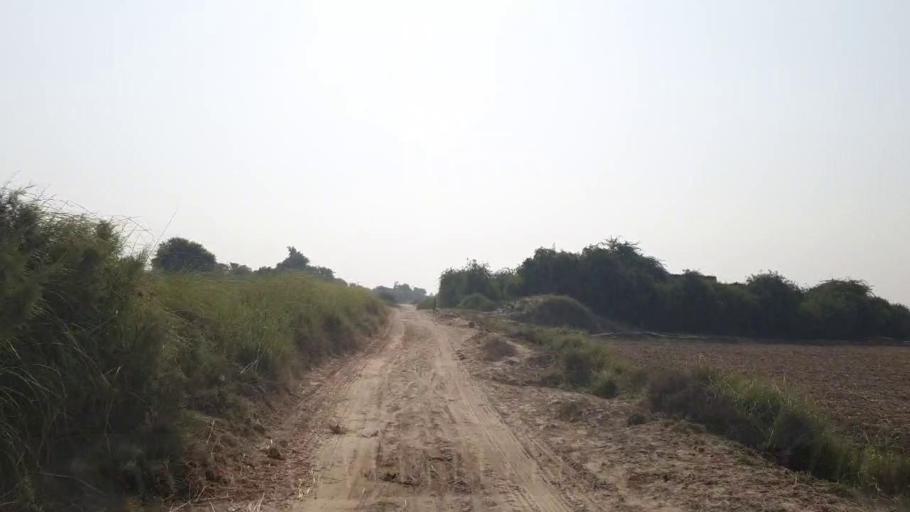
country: PK
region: Sindh
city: Matli
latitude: 24.9560
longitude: 68.6020
